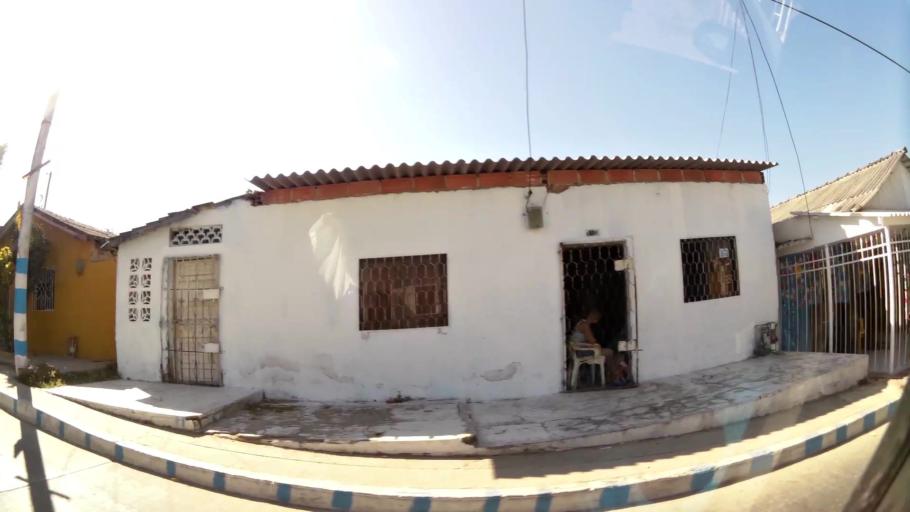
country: CO
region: Atlantico
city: Barranquilla
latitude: 10.9348
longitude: -74.8109
